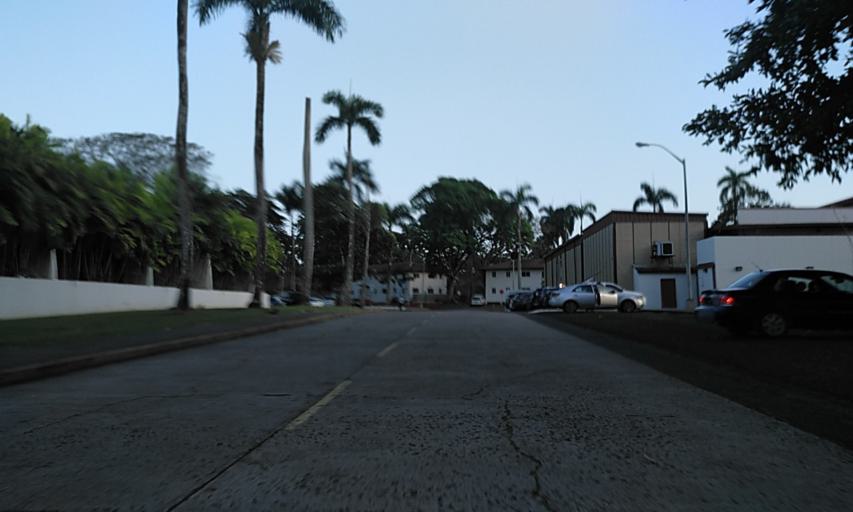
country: PA
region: Panama
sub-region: Distrito de Panama
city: Ancon
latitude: 8.9995
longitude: -79.5818
